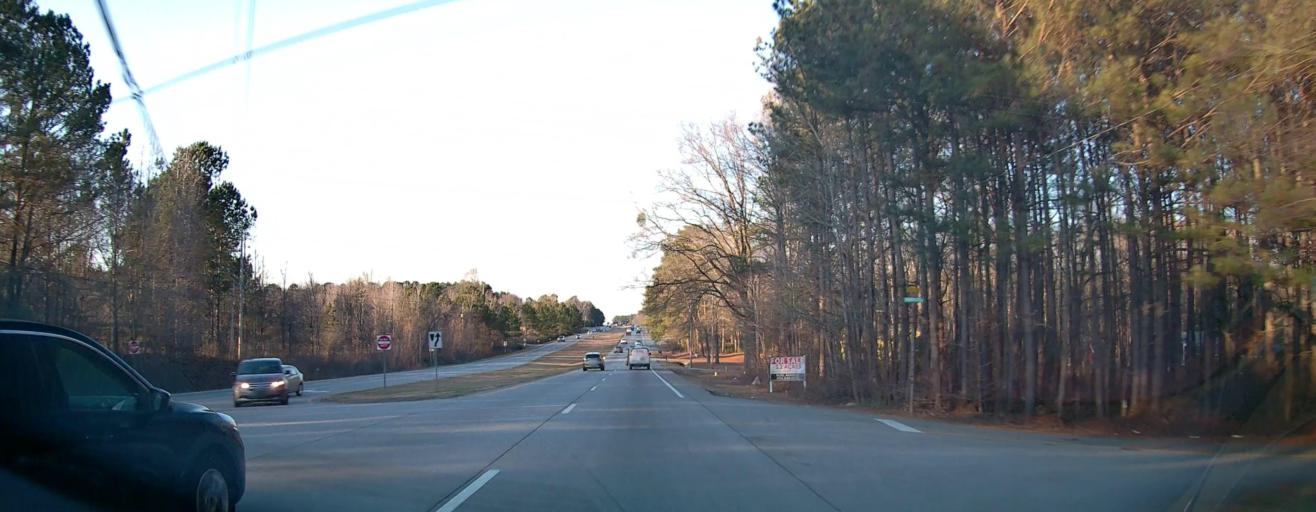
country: US
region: Georgia
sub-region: Fulton County
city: Fairburn
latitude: 33.5214
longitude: -84.5761
